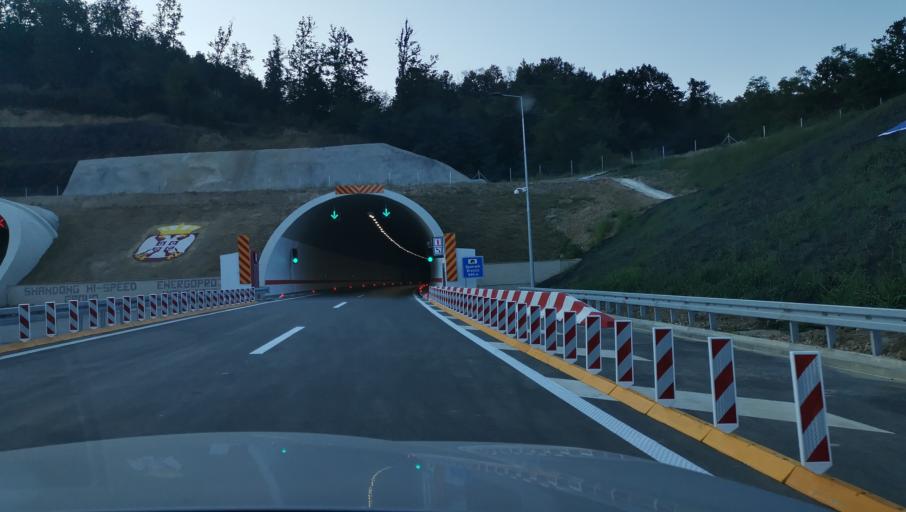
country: RS
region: Central Serbia
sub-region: Kolubarski Okrug
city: Ljig
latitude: 44.2026
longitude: 20.2663
